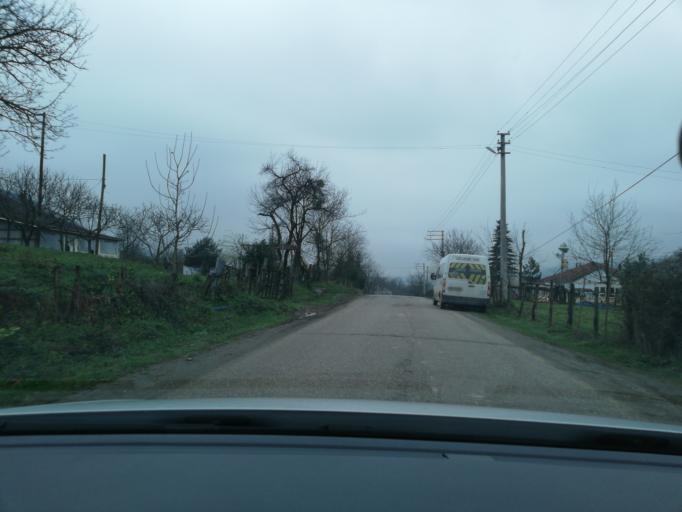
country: TR
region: Duzce
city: Kaynasli
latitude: 40.7735
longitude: 31.3472
